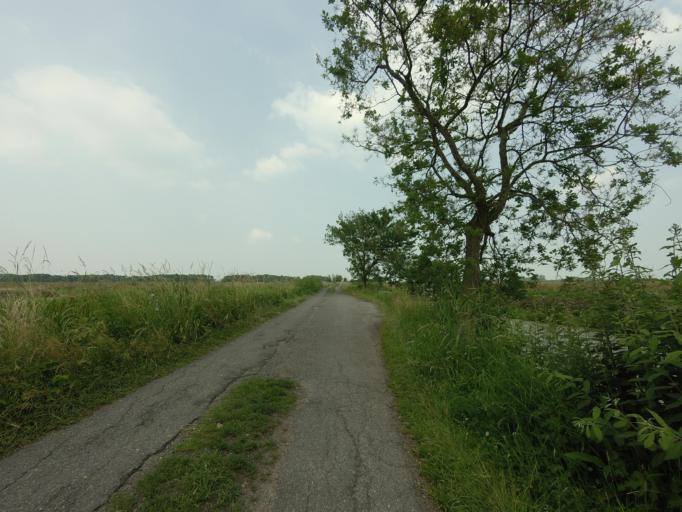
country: NL
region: South Holland
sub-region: Gemeente Gouda
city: Gouda
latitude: 51.9803
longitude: 4.6914
